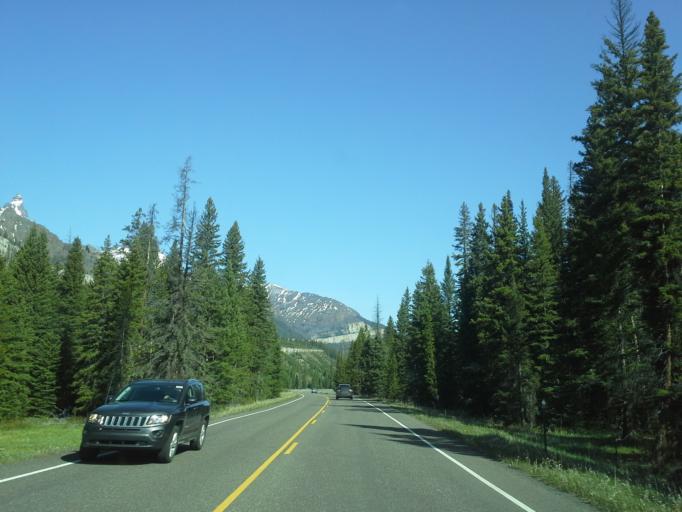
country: US
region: Montana
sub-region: Carbon County
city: Red Lodge
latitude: 44.9602
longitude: -109.8173
